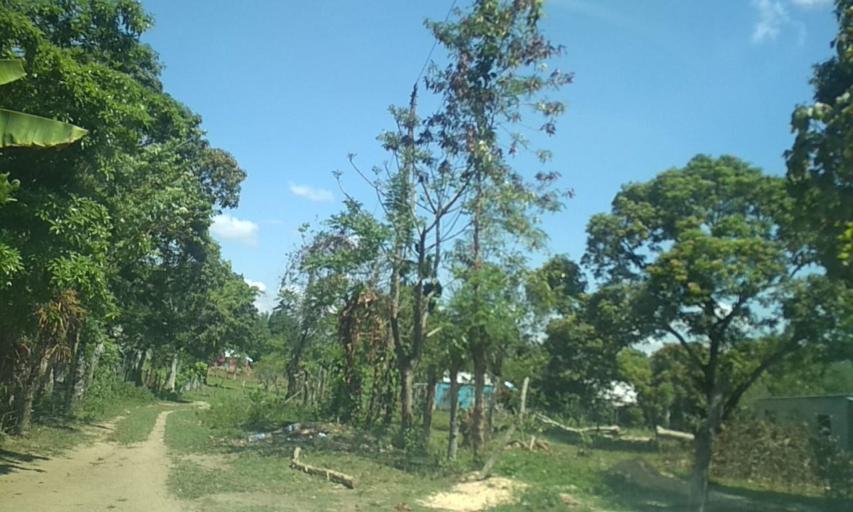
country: MX
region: Veracruz
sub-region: Moloacan
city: Cuichapa
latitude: 17.7858
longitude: -94.1932
